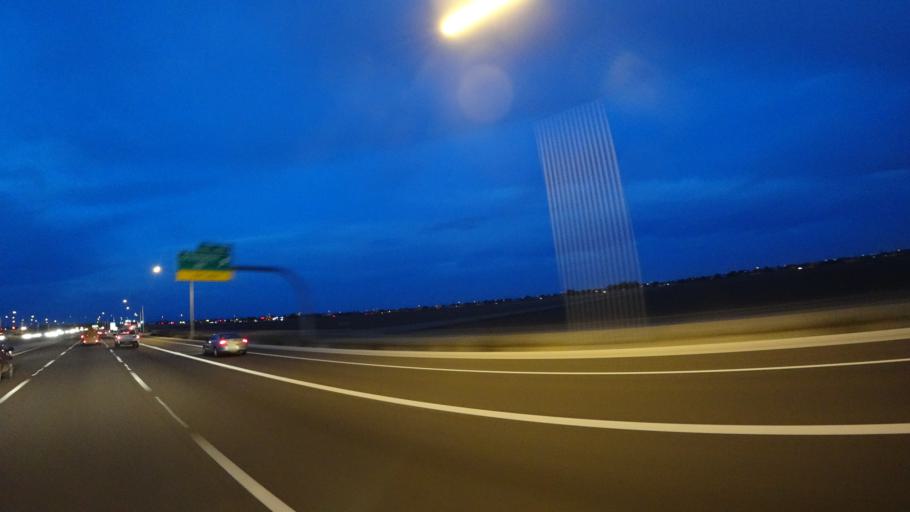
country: US
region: Arizona
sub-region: Maricopa County
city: Citrus Park
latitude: 33.6183
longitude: -112.4179
